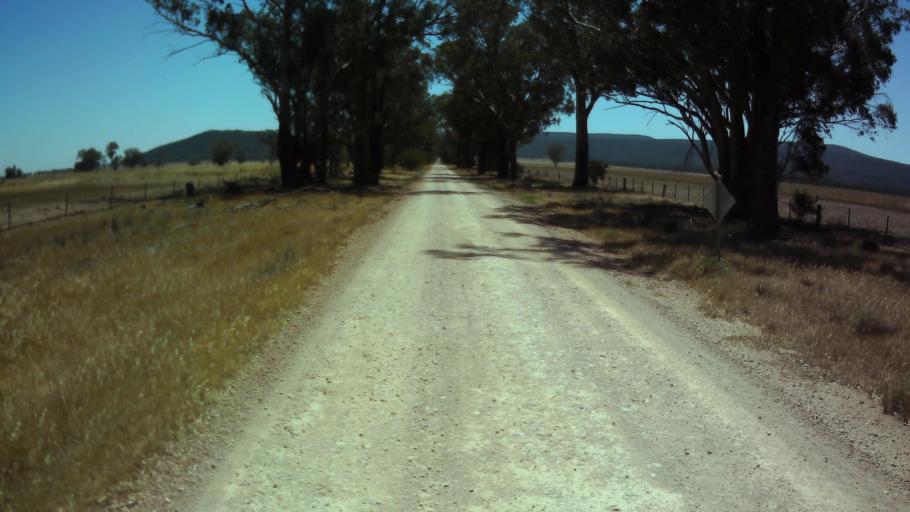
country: AU
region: New South Wales
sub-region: Weddin
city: Grenfell
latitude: -34.0048
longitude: 147.9561
